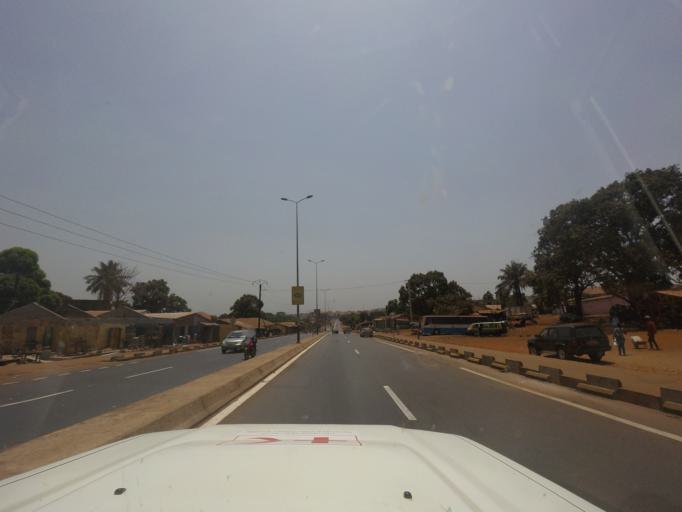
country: GN
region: Kindia
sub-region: Prefecture de Dubreka
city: Dubreka
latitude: 9.6662
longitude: -13.5267
